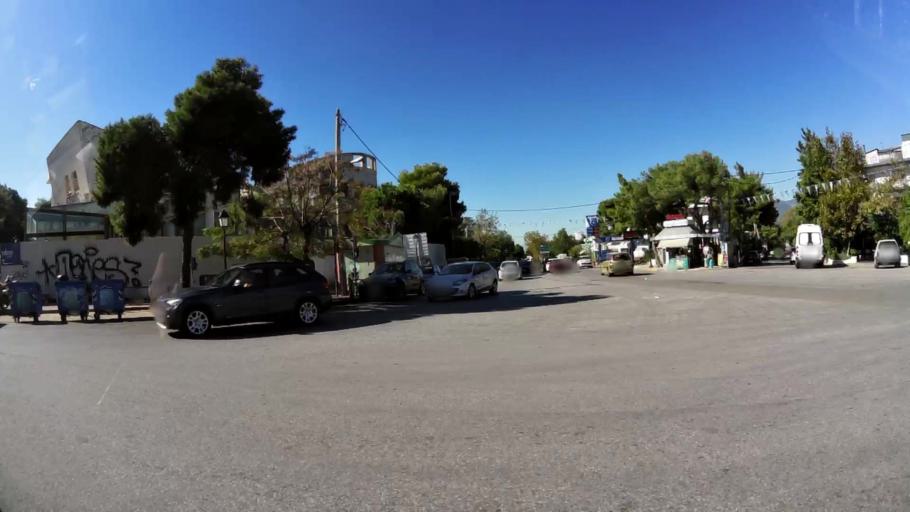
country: GR
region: Attica
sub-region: Nomarchia Athinas
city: Nea Erythraia
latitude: 38.0919
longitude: 23.7960
